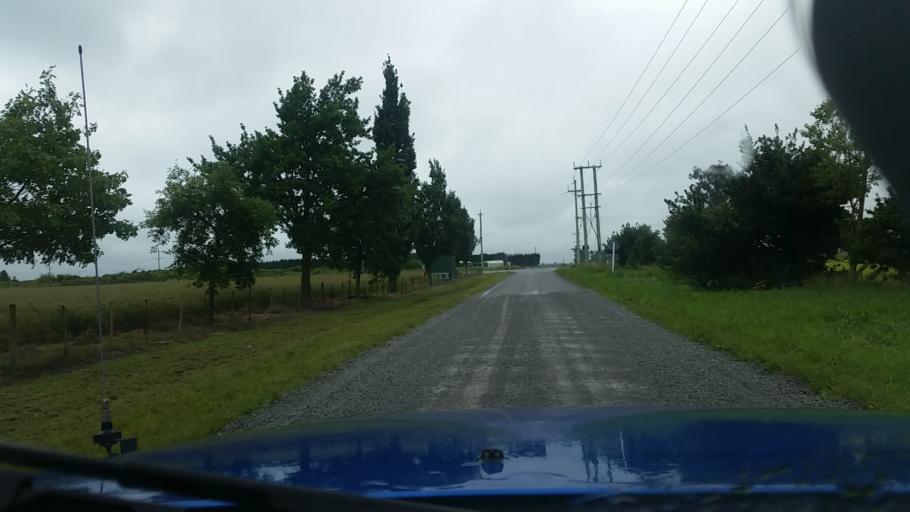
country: NZ
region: Canterbury
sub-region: Ashburton District
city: Tinwald
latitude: -43.8852
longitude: 171.5147
